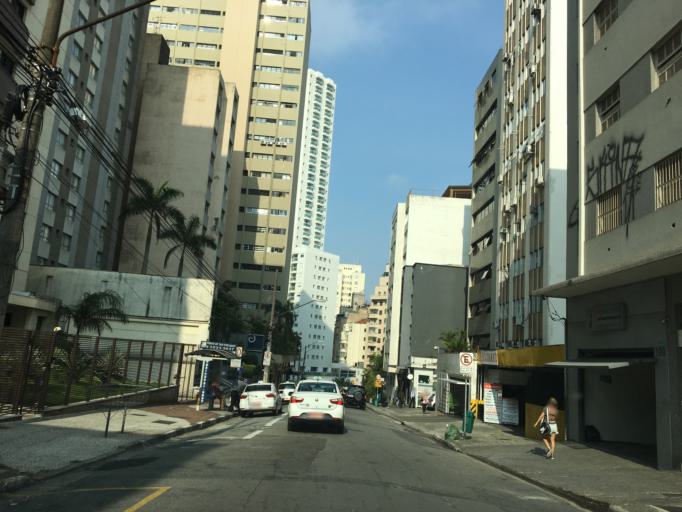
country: BR
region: Sao Paulo
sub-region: Sao Paulo
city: Sao Paulo
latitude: -23.5517
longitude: -46.6490
